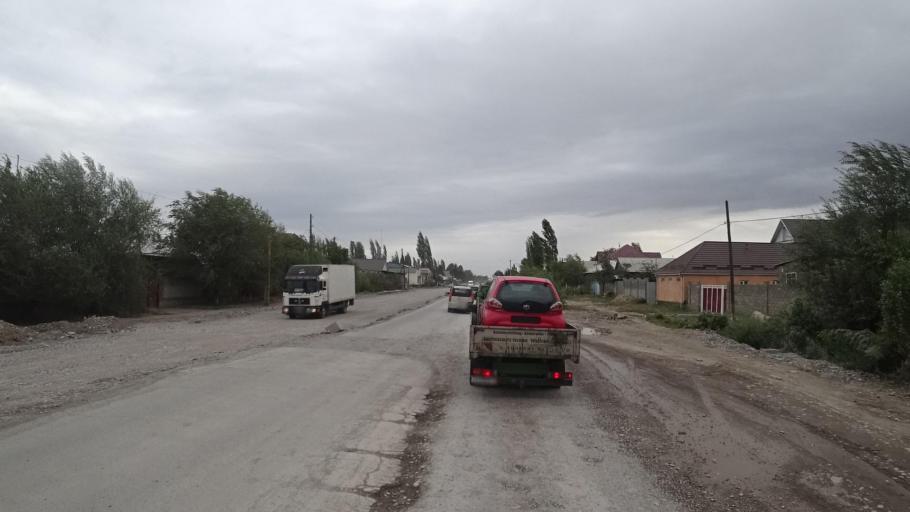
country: KG
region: Chuy
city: Belovodskoye
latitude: 42.8525
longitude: 74.1904
